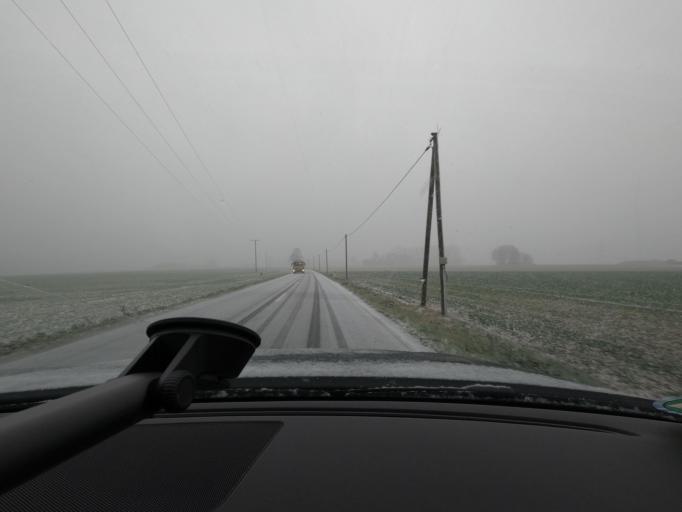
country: DE
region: North Rhine-Westphalia
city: Marsberg
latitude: 51.5294
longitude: 8.8436
